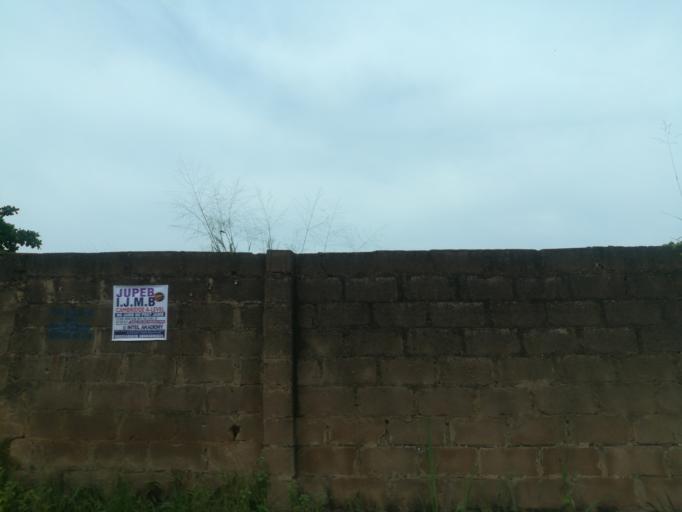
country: NG
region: Oyo
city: Ibadan
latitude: 7.4289
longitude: 3.9125
